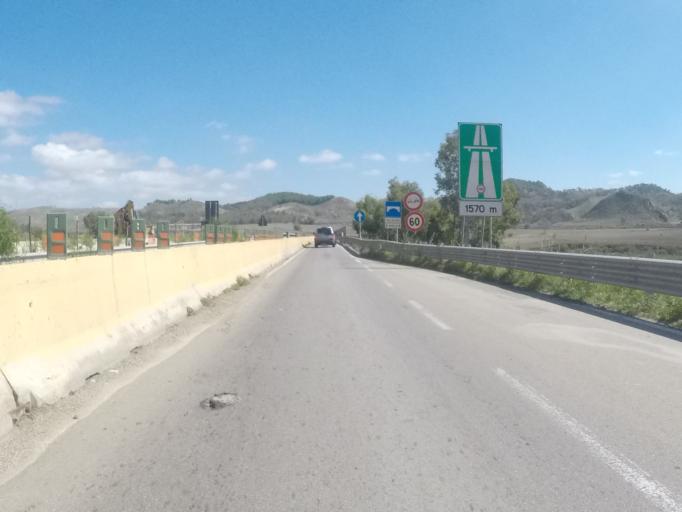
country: IT
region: Sicily
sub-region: Enna
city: Villarosa
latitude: 37.5379
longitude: 14.1307
